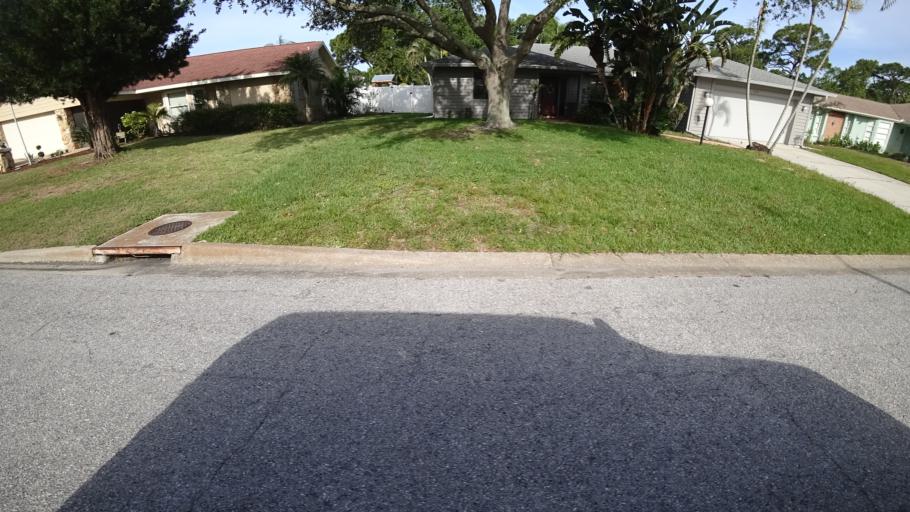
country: US
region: Florida
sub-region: Manatee County
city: West Bradenton
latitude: 27.5015
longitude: -82.6341
